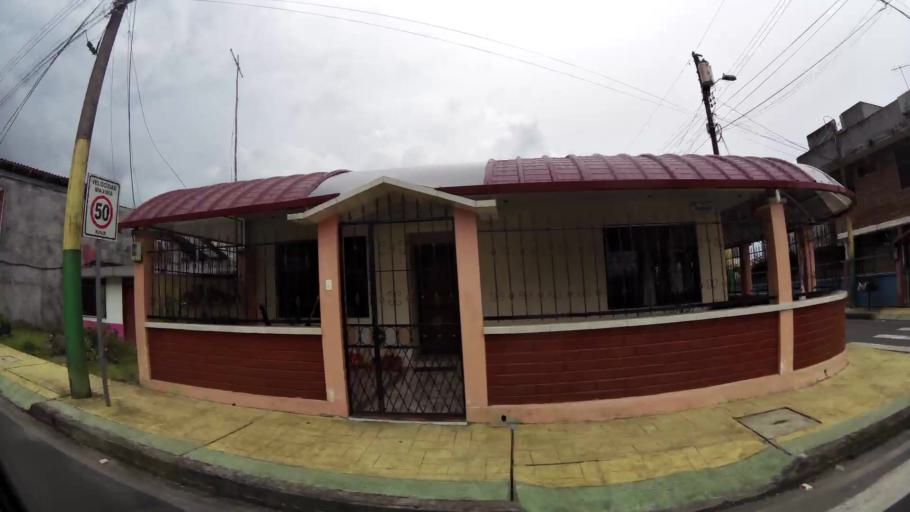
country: EC
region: Pastaza
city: Puyo
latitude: -1.4926
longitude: -78.0100
